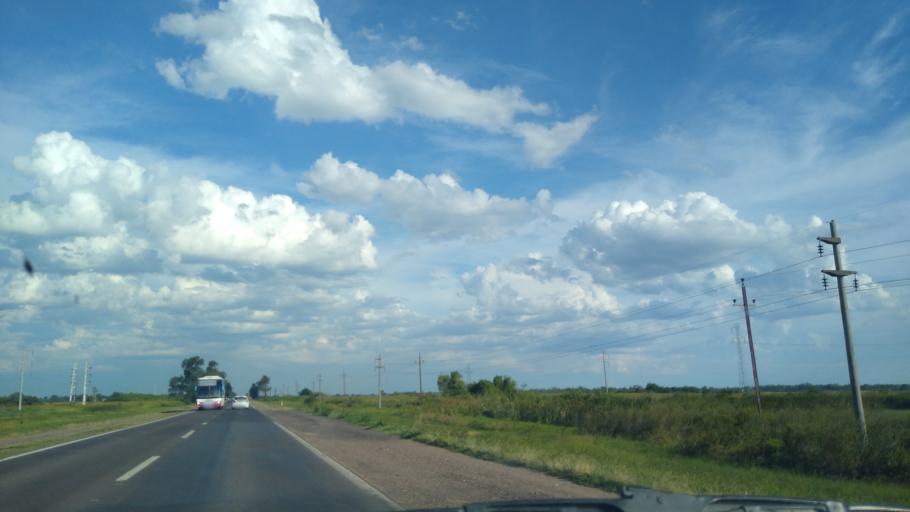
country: AR
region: Chaco
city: Presidencia Roque Saenz Pena
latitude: -26.8178
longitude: -60.4035
